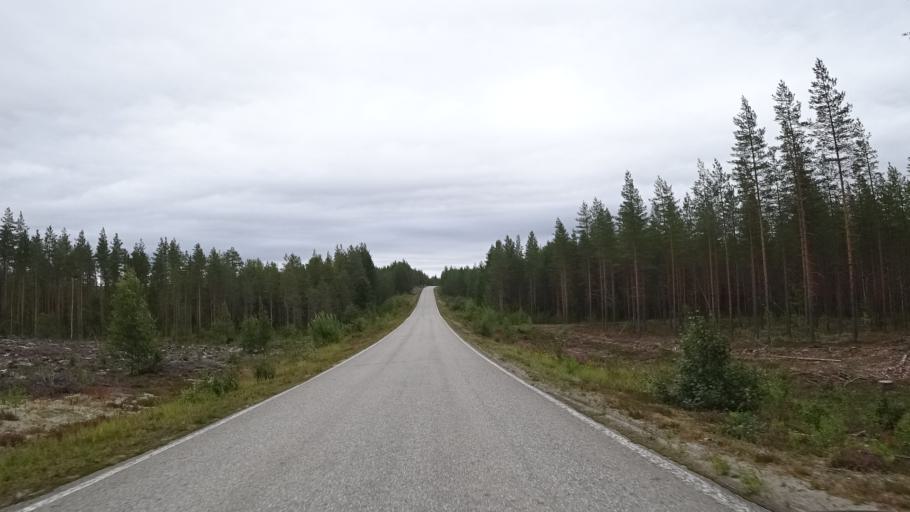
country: FI
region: North Karelia
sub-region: Pielisen Karjala
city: Lieksa
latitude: 63.3798
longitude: 30.3170
